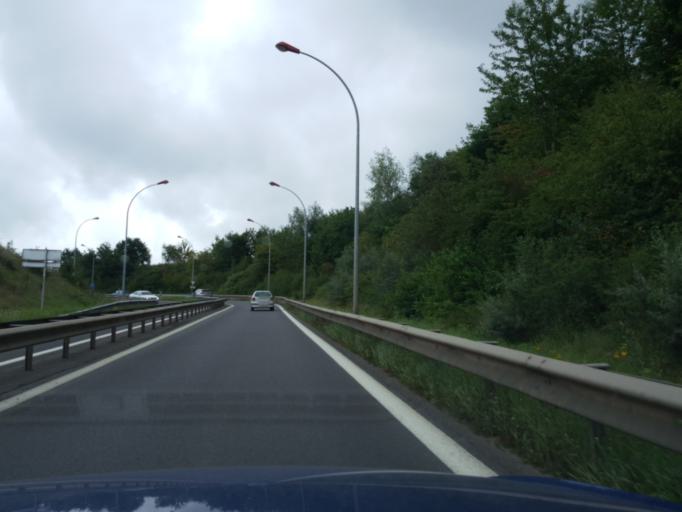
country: LU
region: Luxembourg
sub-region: Canton de Mersch
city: Mersch
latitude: 49.7620
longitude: 6.0902
